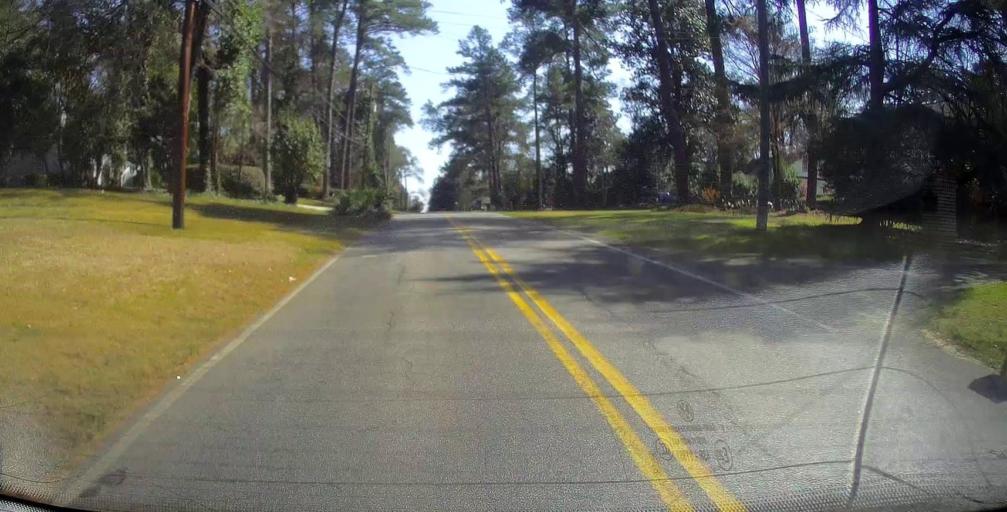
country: US
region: Georgia
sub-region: Bibb County
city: Macon
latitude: 32.8562
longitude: -83.6306
